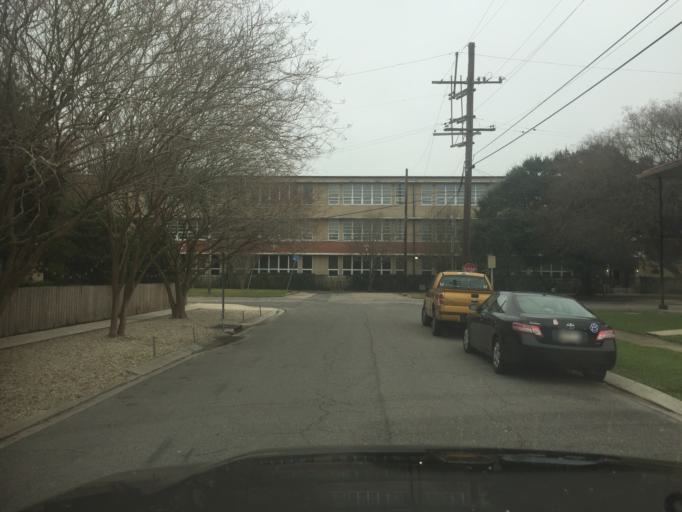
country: US
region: Louisiana
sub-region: Jefferson Parish
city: Metairie
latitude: 30.0191
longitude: -90.1113
